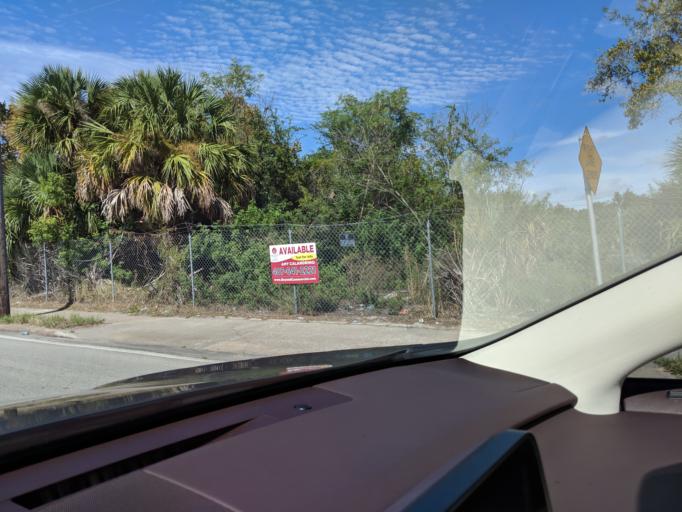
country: US
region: Florida
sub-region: Orange County
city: Fairview Shores
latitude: 28.5782
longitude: -81.4075
